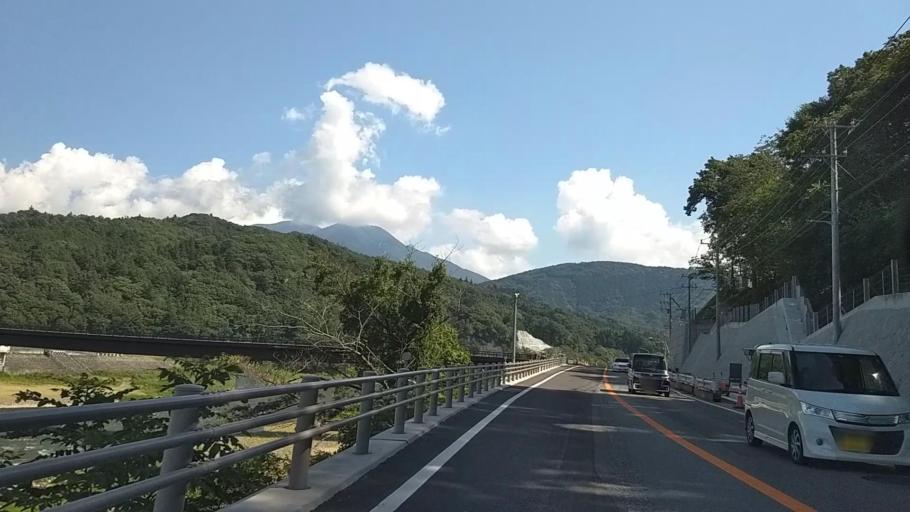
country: JP
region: Yamanashi
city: Ryuo
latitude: 35.4573
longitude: 138.4440
